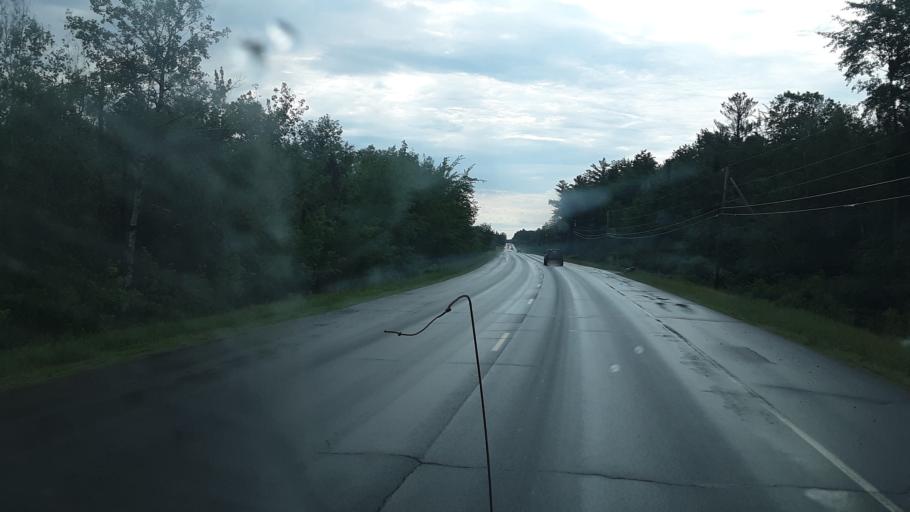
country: US
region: Maine
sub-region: Penobscot County
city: Milford
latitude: 44.9463
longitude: -68.6872
